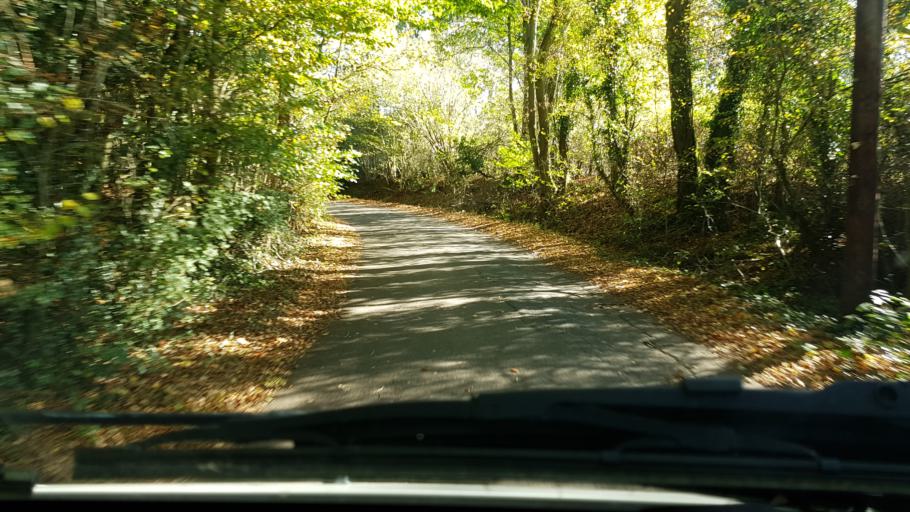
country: GB
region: England
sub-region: Surrey
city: Ockley
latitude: 51.1242
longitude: -0.3574
